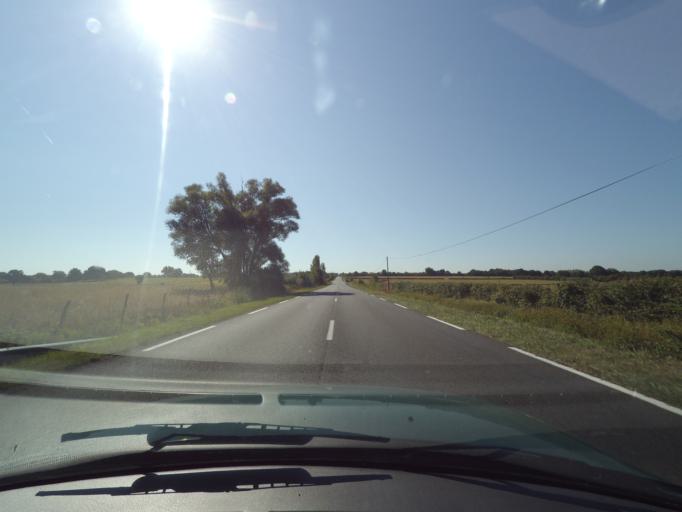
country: FR
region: Poitou-Charentes
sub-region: Departement de la Vienne
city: Lussac-les-Chateaux
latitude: 46.3735
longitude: 0.7600
